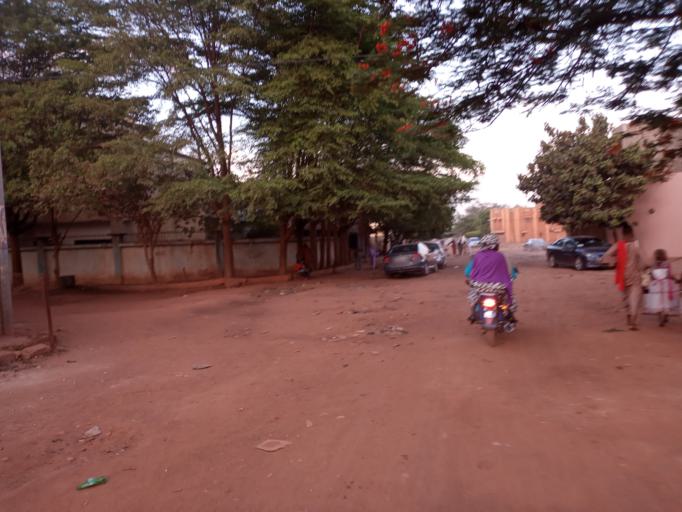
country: ML
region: Bamako
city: Bamako
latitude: 12.5696
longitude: -7.9851
